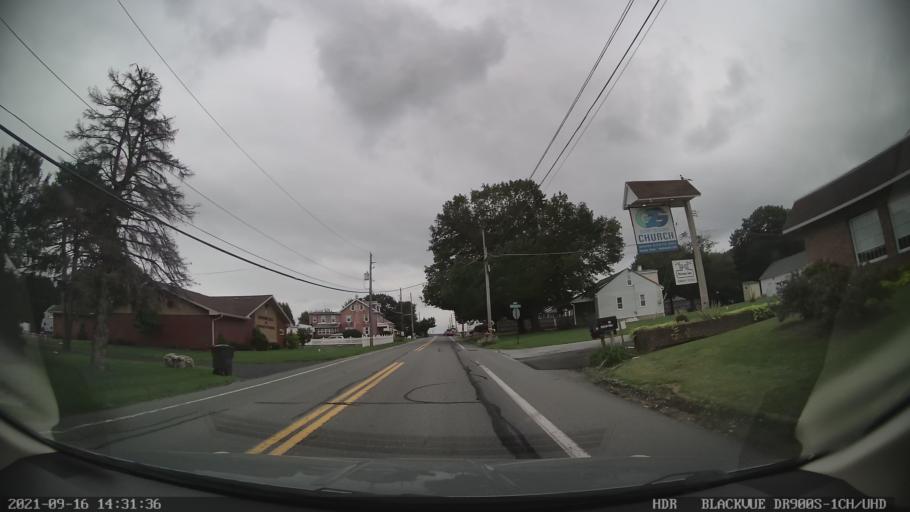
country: US
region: Pennsylvania
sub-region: Berks County
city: Kutztown
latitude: 40.5049
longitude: -75.7690
